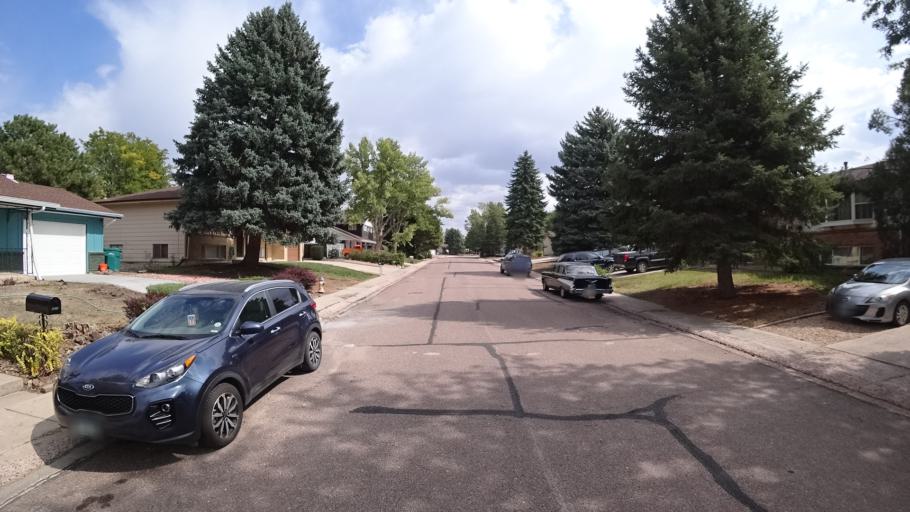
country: US
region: Colorado
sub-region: El Paso County
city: Cimarron Hills
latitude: 38.8488
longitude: -104.7417
